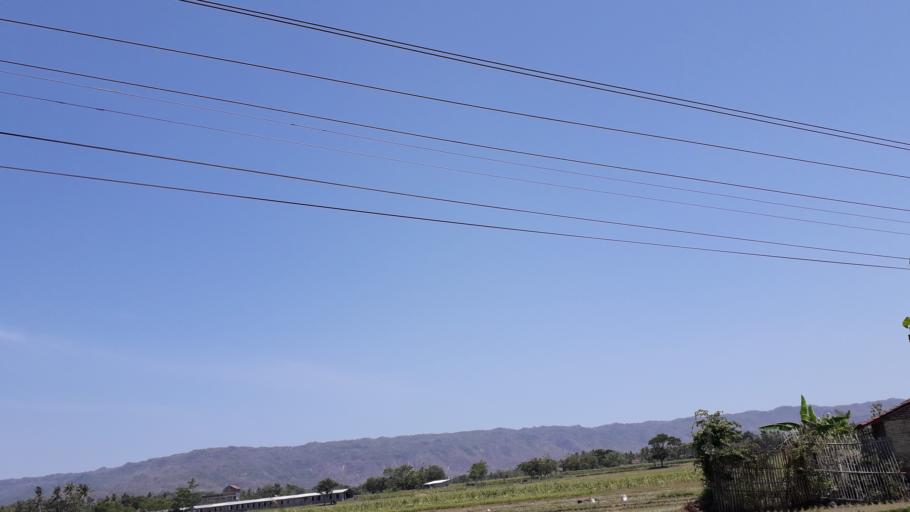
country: ID
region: Daerah Istimewa Yogyakarta
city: Pundong
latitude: -7.9349
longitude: 110.3424
